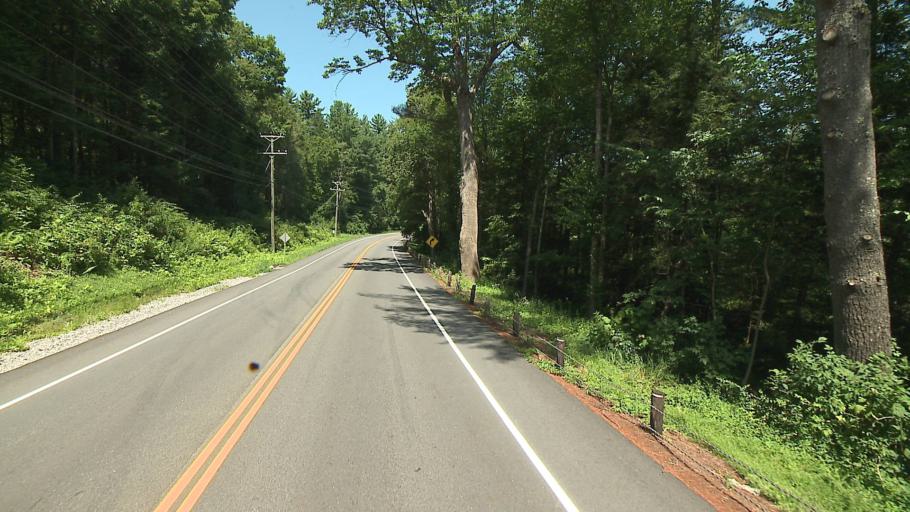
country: US
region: Connecticut
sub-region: Litchfield County
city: New Preston
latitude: 41.8371
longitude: -73.3489
